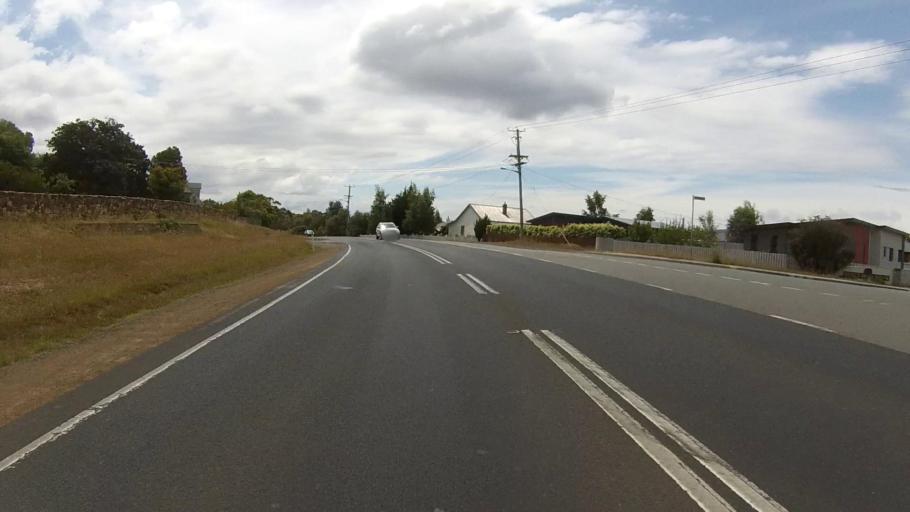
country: AU
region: Tasmania
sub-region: Kingborough
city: Margate
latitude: -43.0543
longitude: 147.2621
